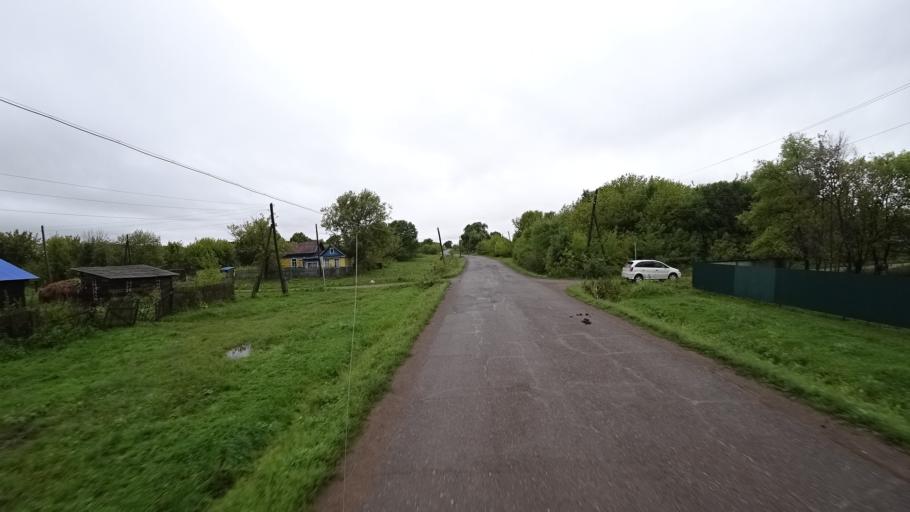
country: RU
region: Primorskiy
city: Monastyrishche
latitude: 44.2564
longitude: 132.4251
